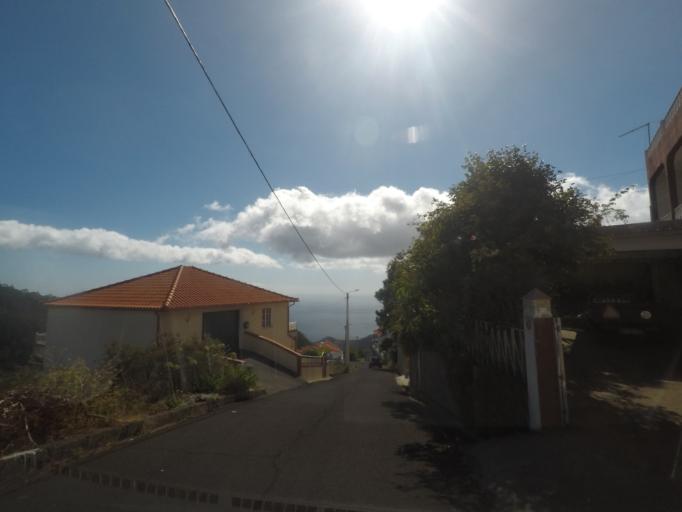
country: PT
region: Madeira
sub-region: Ribeira Brava
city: Campanario
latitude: 32.6936
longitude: -17.0346
